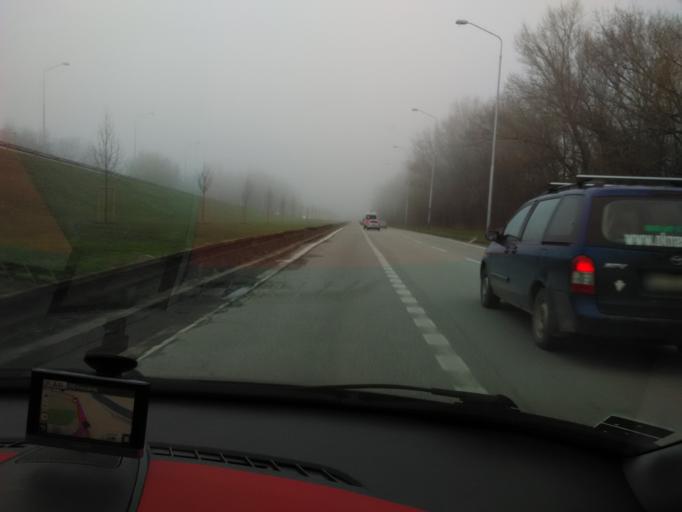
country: SK
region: Bratislavsky
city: Bratislava
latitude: 48.1125
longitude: 17.1294
